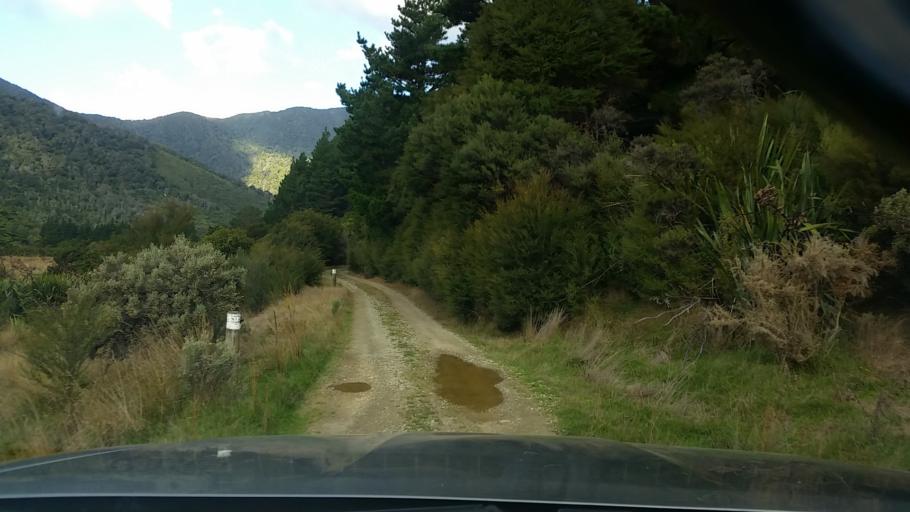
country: NZ
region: Marlborough
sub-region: Marlborough District
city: Picton
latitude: -41.0616
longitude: 174.1168
